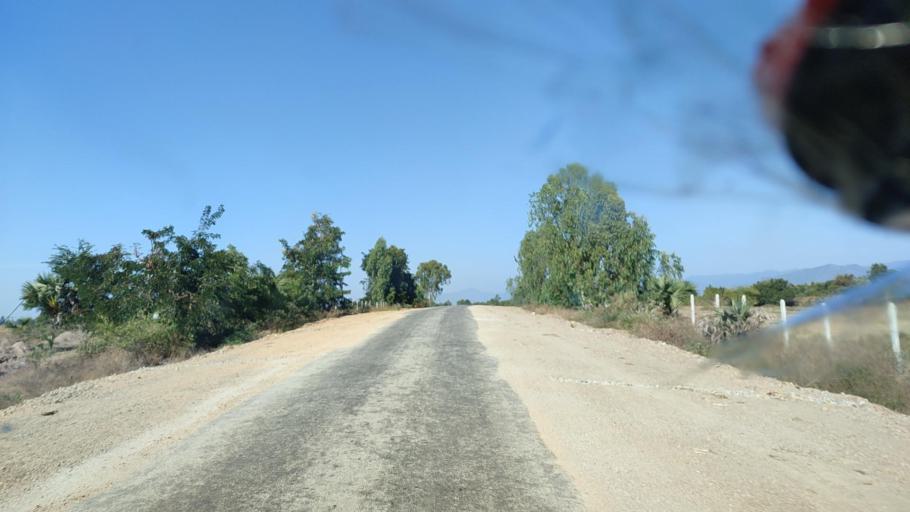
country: MM
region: Mandalay
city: Yamethin
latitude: 20.0954
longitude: 96.2654
